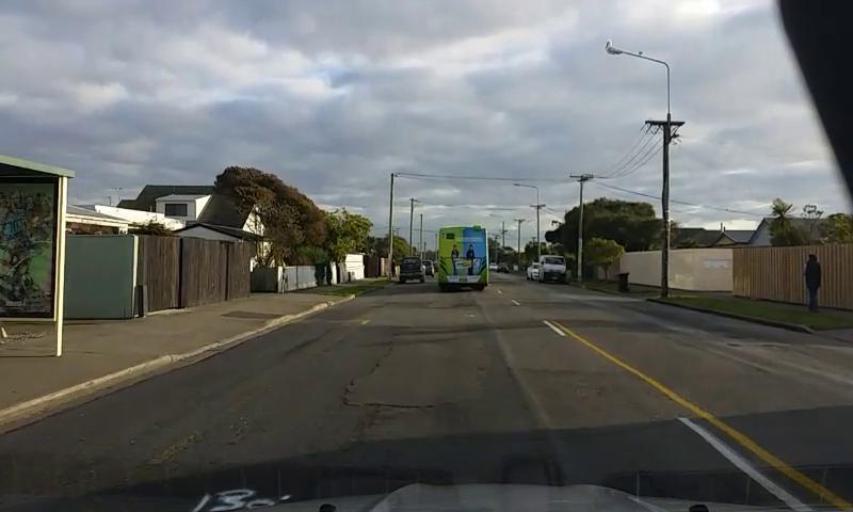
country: NZ
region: Canterbury
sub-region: Christchurch City
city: Christchurch
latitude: -43.5230
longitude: 172.7325
